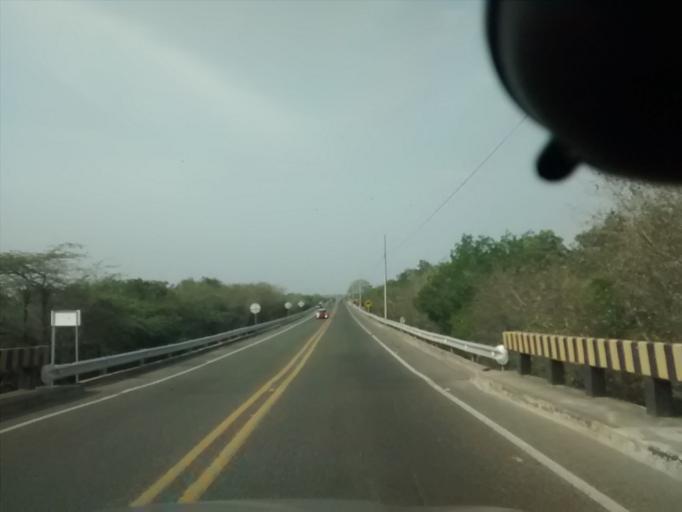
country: CO
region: Bolivar
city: Cartagena
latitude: 10.4896
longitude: -75.4833
